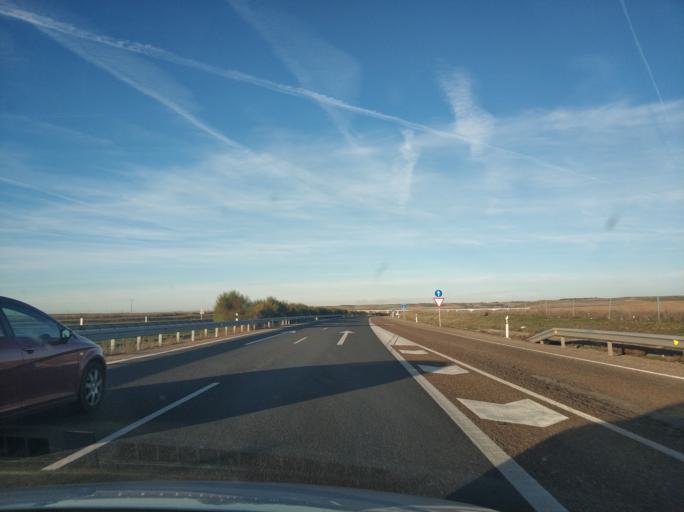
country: ES
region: Castille and Leon
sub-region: Provincia de Valladolid
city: Siete Iglesias de Trabancos
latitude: 41.3622
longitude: -5.1670
